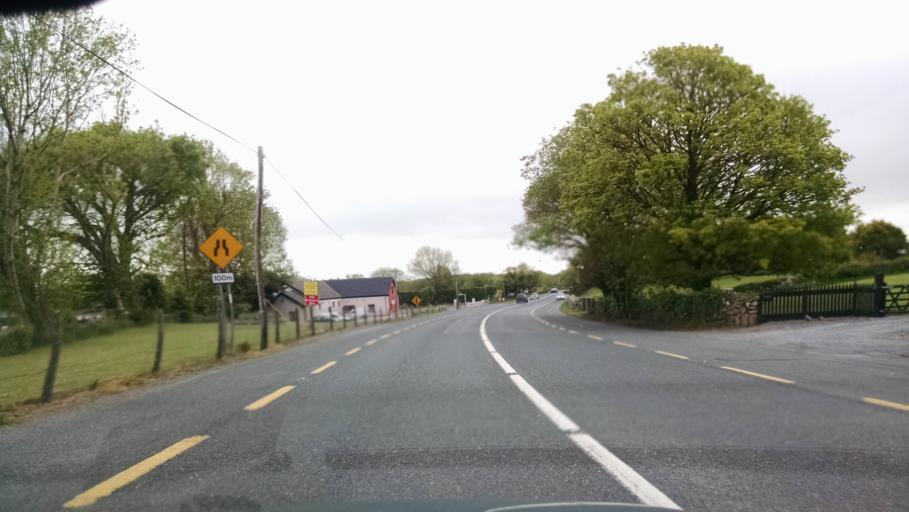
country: IE
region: Connaught
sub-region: County Galway
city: Moycullen
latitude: 53.4467
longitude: -9.0860
